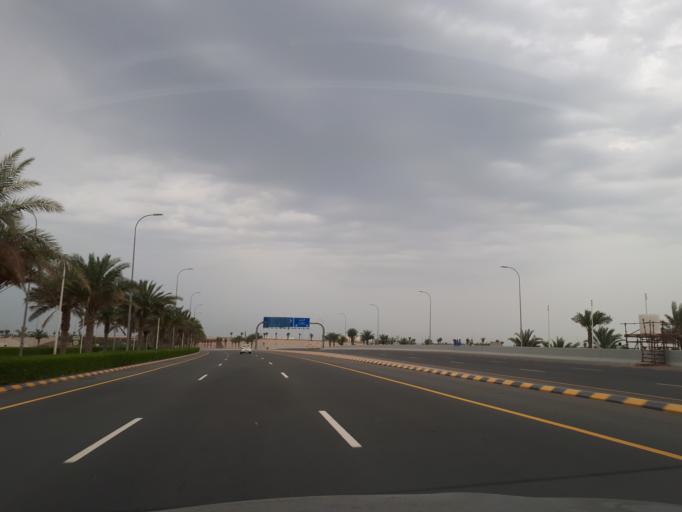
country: OM
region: Muhafazat Masqat
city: Bawshar
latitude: 23.5936
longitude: 58.3322
